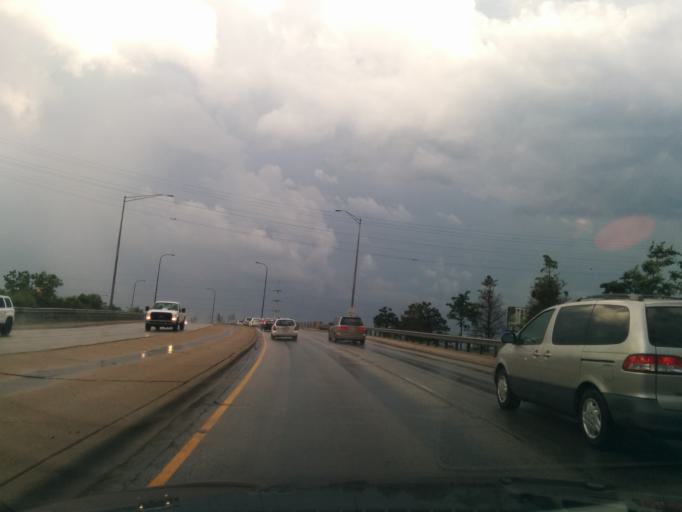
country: US
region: Illinois
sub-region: Cook County
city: Summit
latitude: 41.7706
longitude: -87.8048
